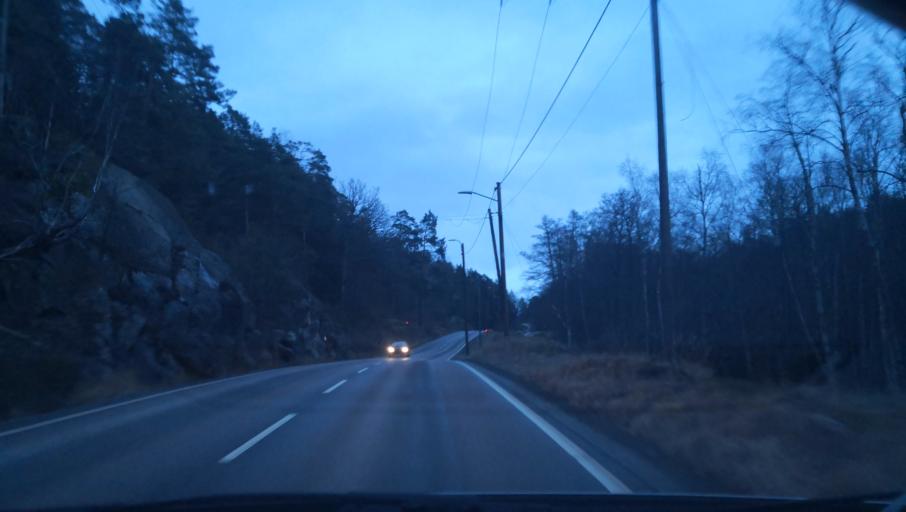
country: SE
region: Stockholm
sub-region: Varmdo Kommun
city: Gustavsberg
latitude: 59.3313
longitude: 18.3492
